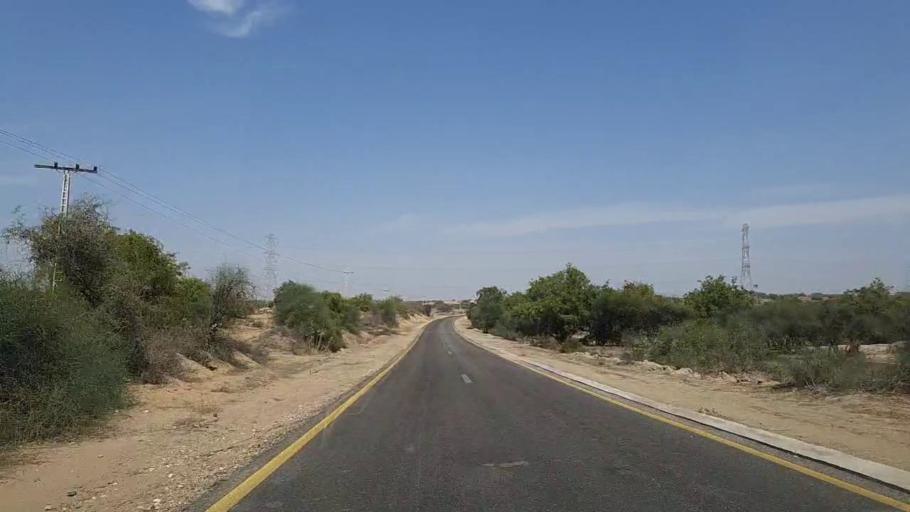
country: PK
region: Sindh
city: Mithi
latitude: 24.8483
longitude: 69.8372
